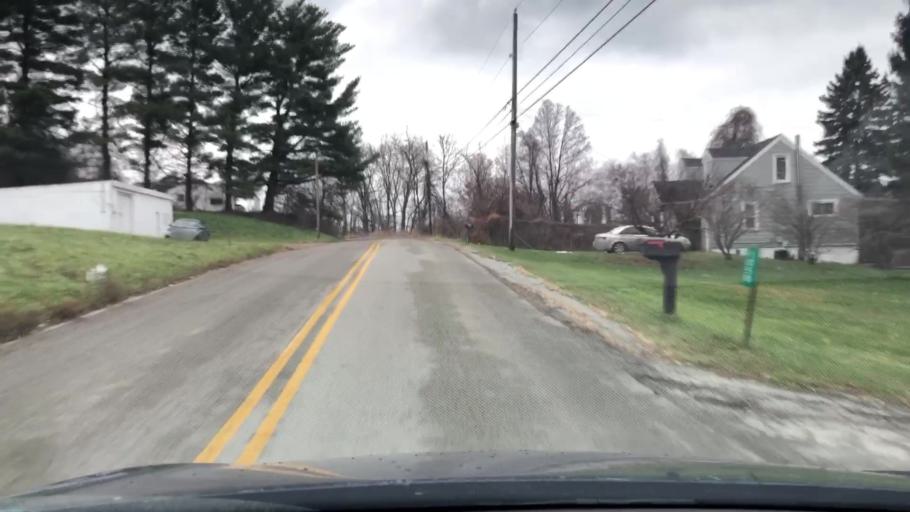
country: US
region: Pennsylvania
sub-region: Fayette County
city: Dunbar
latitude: 39.9816
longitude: -79.6272
